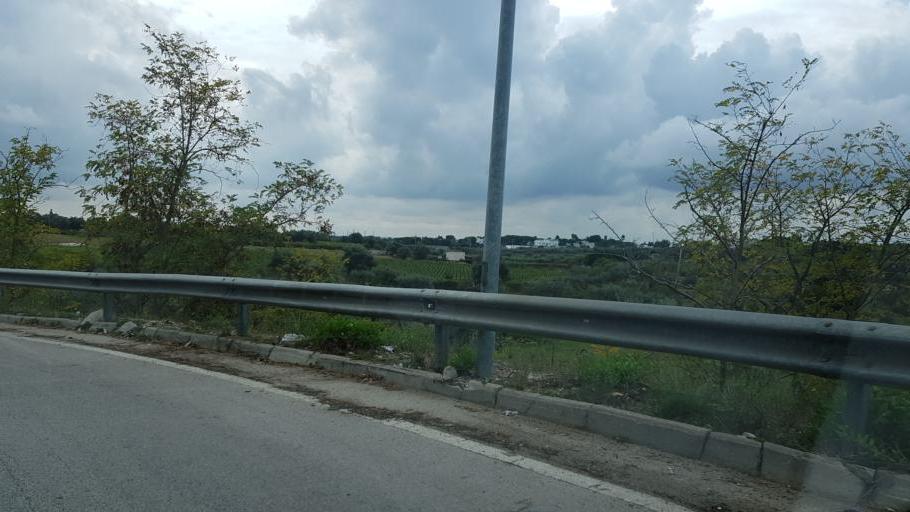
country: IT
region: Apulia
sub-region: Provincia di Bari
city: Triggiano
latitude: 41.0862
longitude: 16.8938
